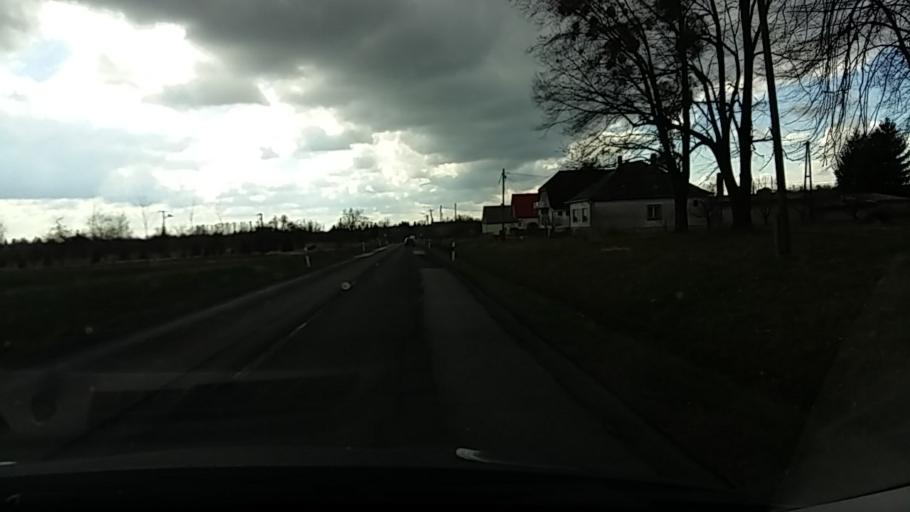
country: HU
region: Somogy
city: Bohonye
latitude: 46.4202
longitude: 17.3818
